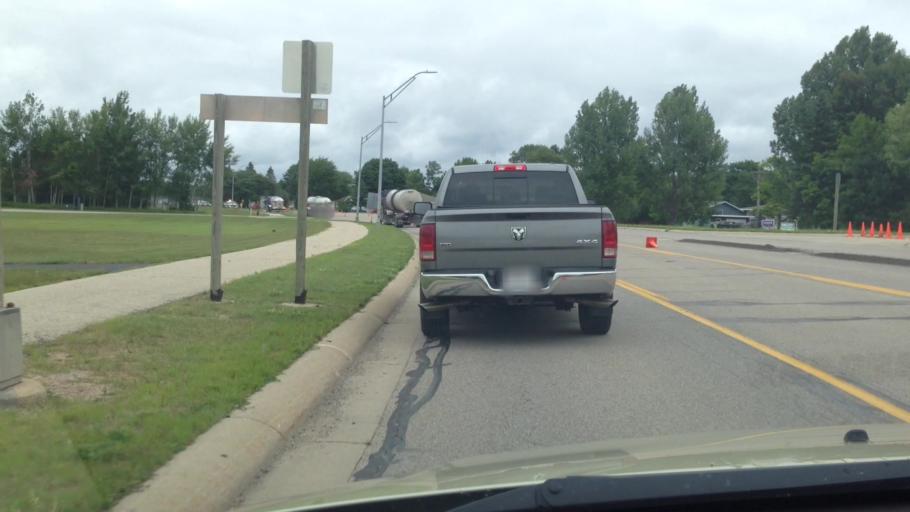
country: US
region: Michigan
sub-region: Delta County
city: Escanaba
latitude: 45.7163
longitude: -87.0809
